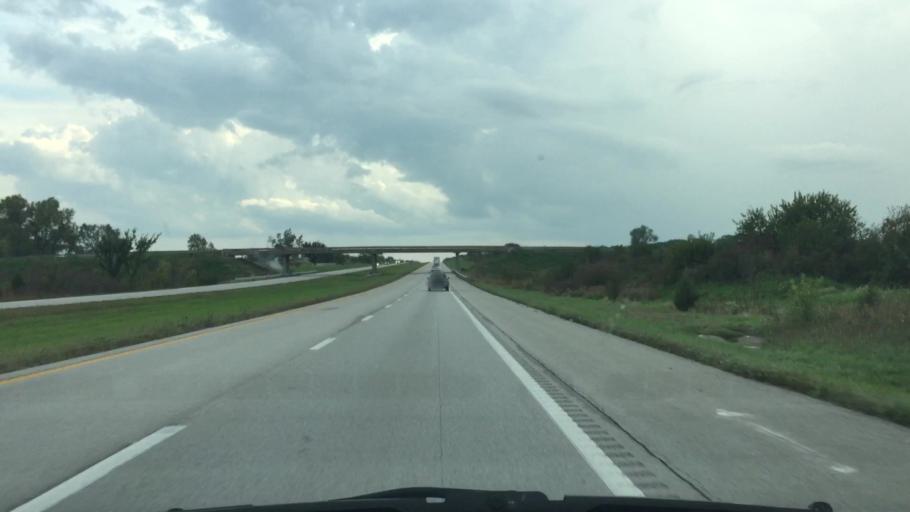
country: US
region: Missouri
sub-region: Clinton County
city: Cameron
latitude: 39.8051
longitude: -94.1983
